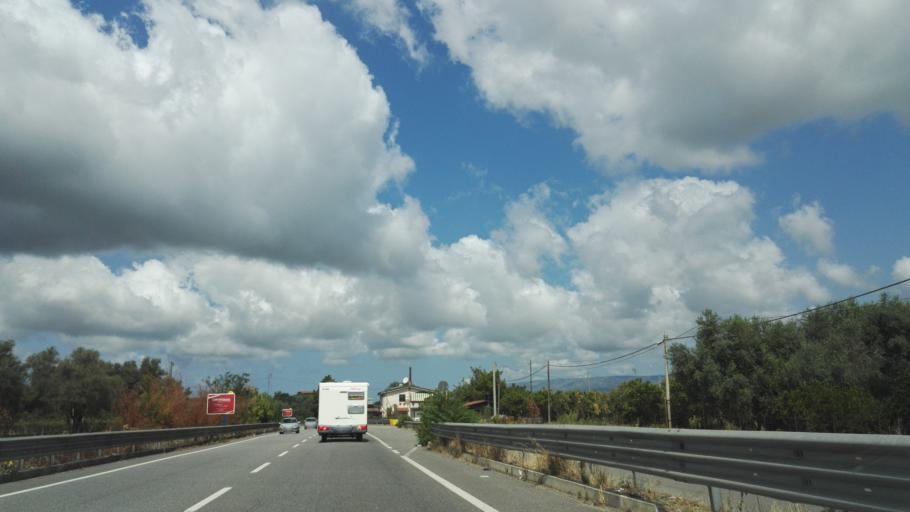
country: IT
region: Calabria
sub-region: Provincia di Reggio Calabria
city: Melicucco
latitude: 38.4573
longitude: 16.0223
